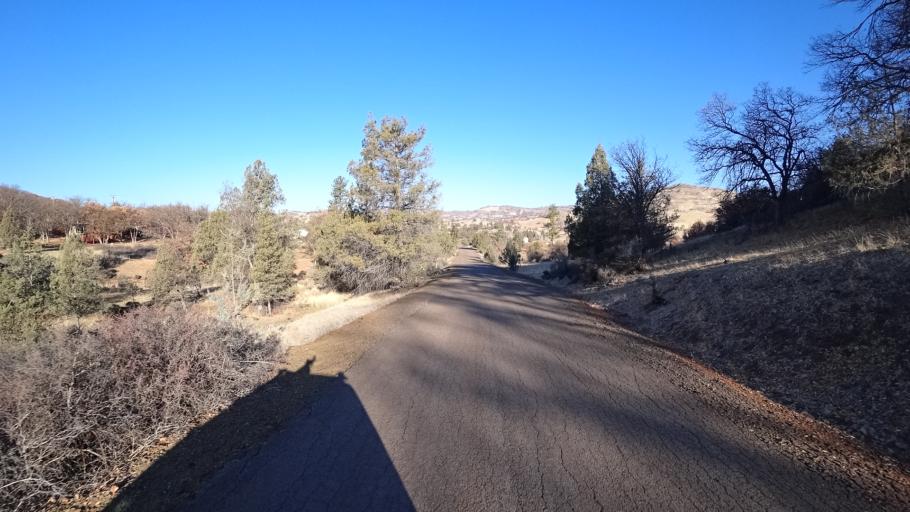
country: US
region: California
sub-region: Siskiyou County
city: Montague
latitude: 41.8940
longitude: -122.5002
